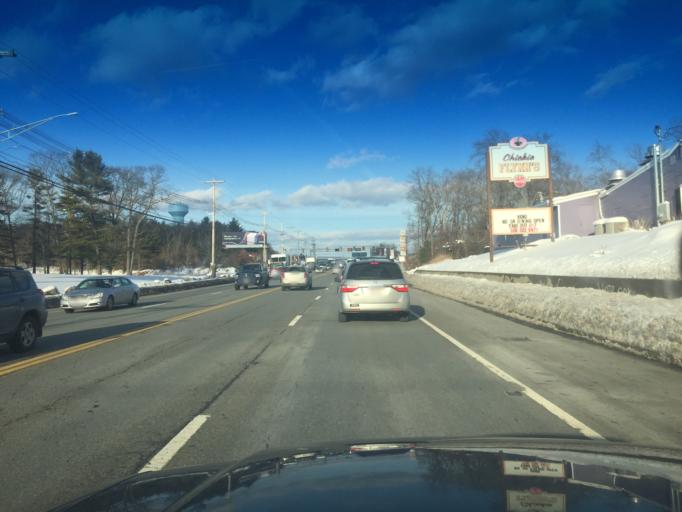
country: US
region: Massachusetts
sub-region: Norfolk County
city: Foxborough
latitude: 42.0847
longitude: -71.2767
